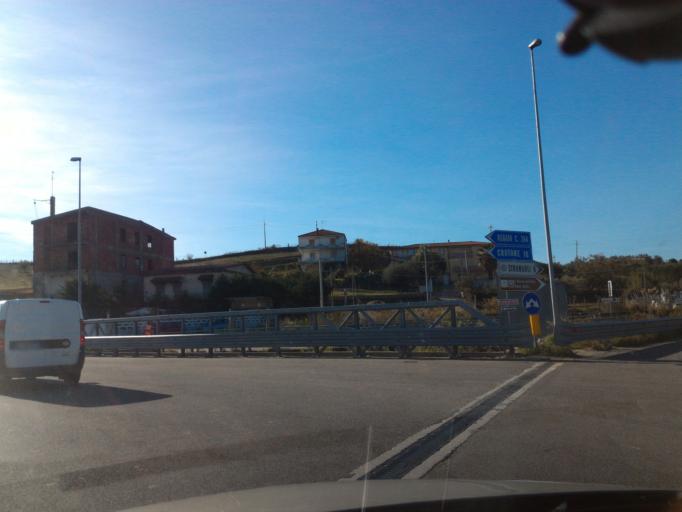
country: IT
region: Calabria
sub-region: Provincia di Crotone
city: Tronca
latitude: 39.2297
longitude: 17.1003
